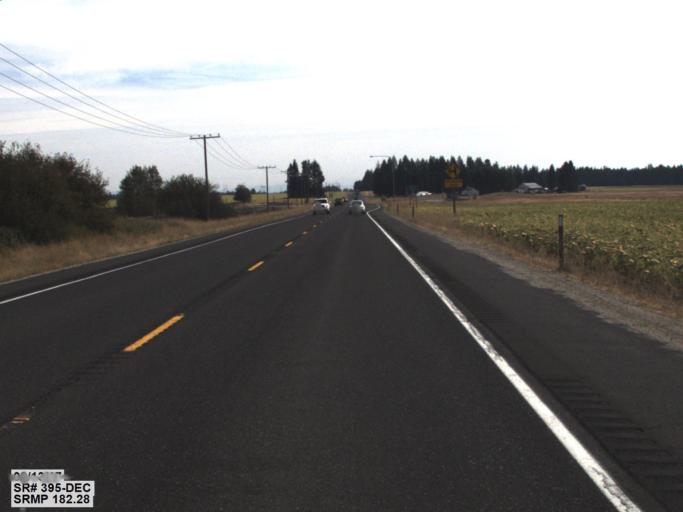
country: US
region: Washington
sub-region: Spokane County
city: Deer Park
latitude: 47.9729
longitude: -117.5153
